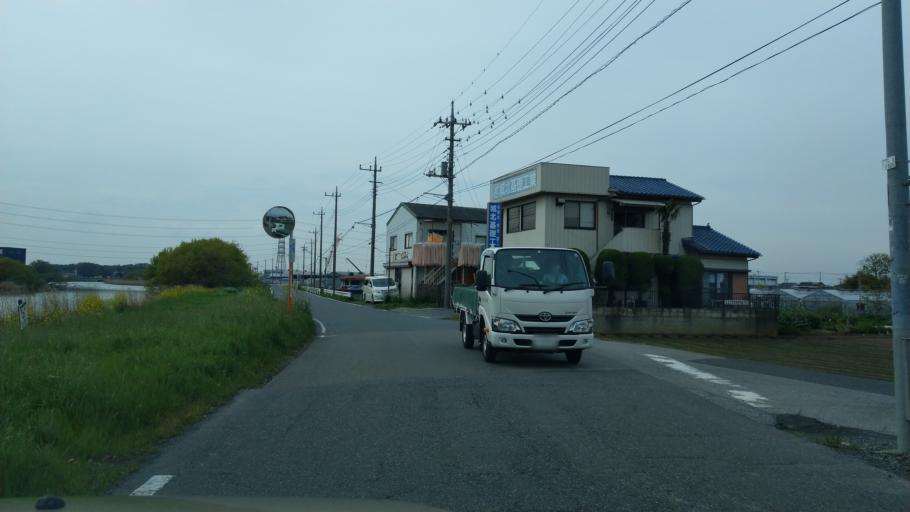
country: JP
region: Saitama
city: Kasukabe
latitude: 35.9447
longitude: 139.7261
